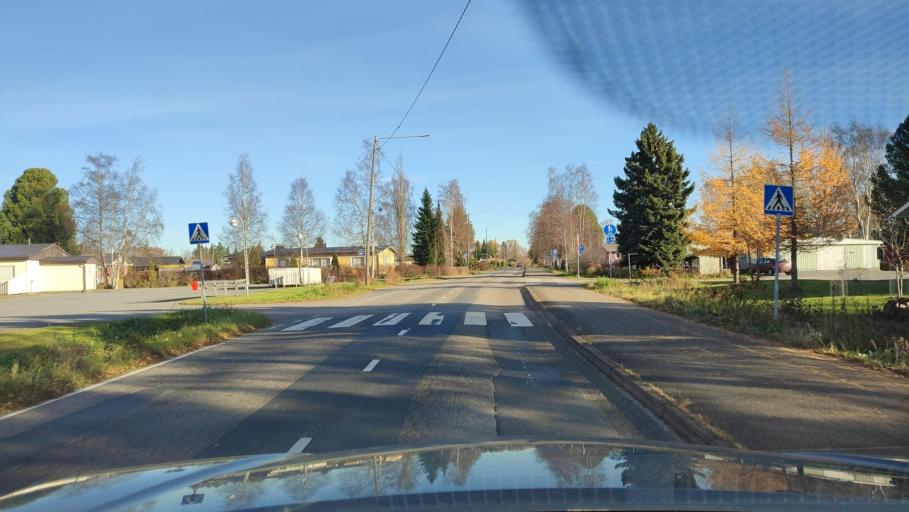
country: FI
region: Southern Ostrobothnia
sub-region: Suupohja
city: Teuva
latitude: 62.4872
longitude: 21.7518
